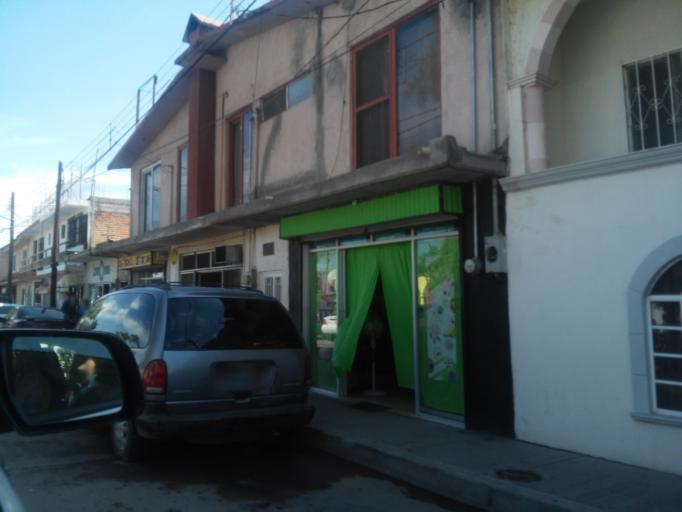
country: MX
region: Durango
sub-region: Santiago Papasquiaro
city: Santiago Papasquiaro
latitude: 25.0485
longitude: -105.4200
